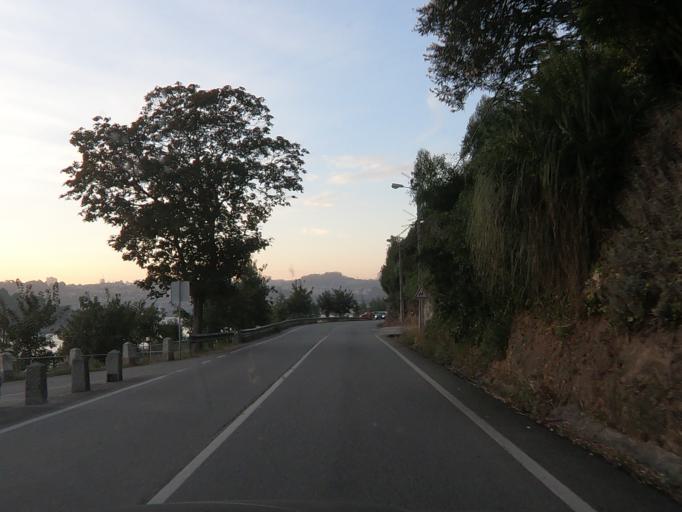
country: PT
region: Porto
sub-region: Gondomar
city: Valbom
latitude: 41.1317
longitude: -8.5688
